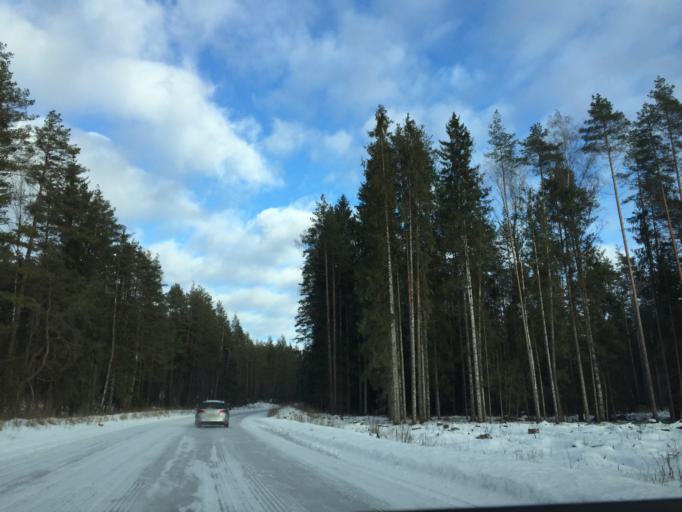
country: LV
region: Ogre
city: Jumprava
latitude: 56.5738
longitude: 24.9381
